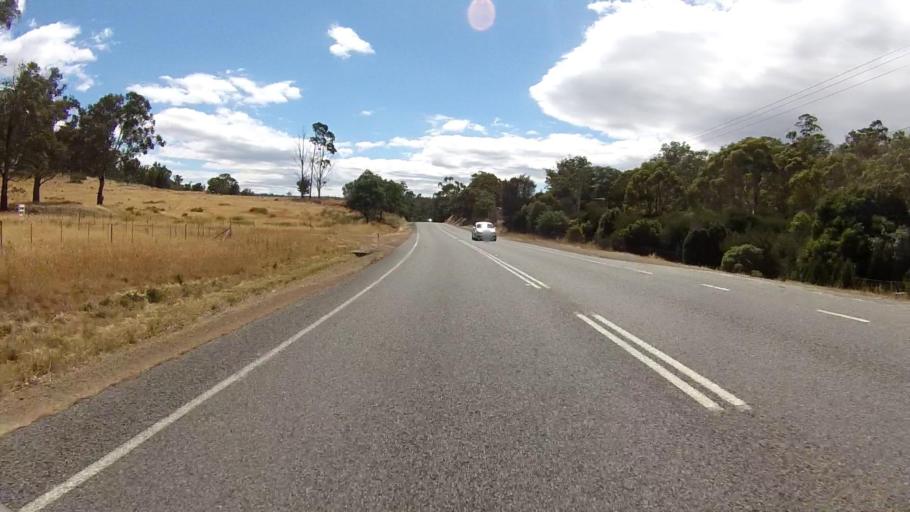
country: AU
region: Tasmania
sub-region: Sorell
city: Sorell
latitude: -42.6099
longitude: 147.6697
